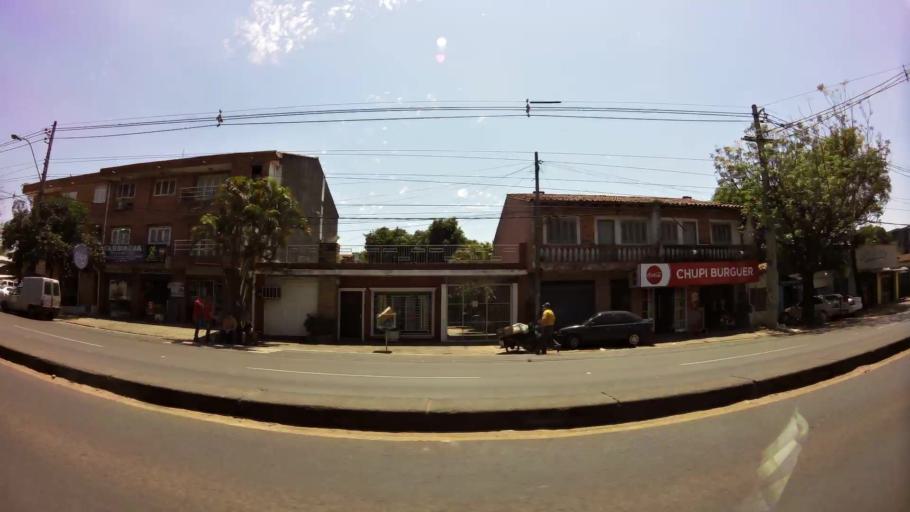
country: PY
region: Central
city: Fernando de la Mora
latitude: -25.3223
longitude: -57.5630
